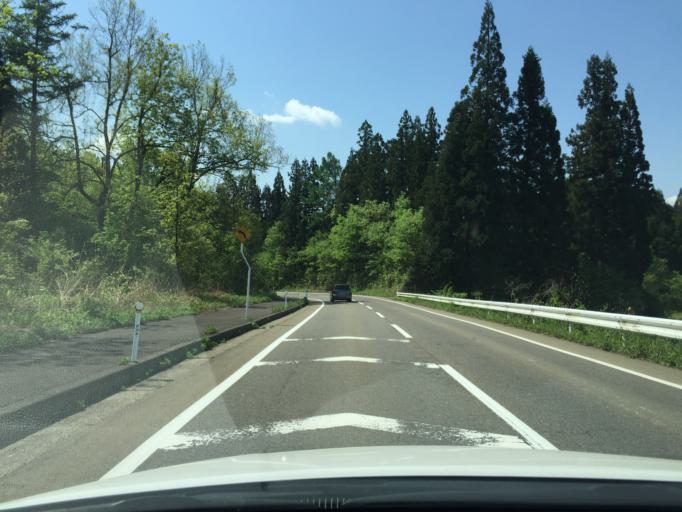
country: JP
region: Niigata
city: Kamo
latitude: 37.5923
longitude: 139.0929
